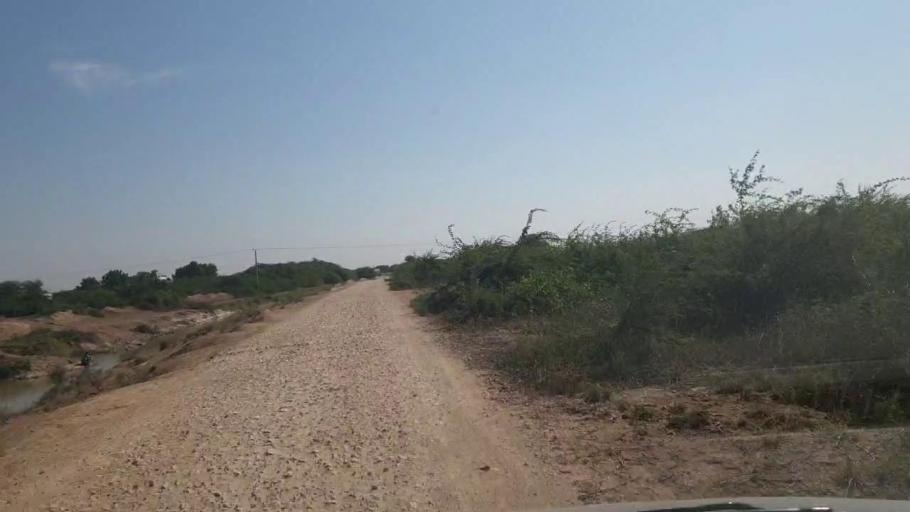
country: PK
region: Sindh
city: Digri
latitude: 24.9446
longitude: 69.1569
